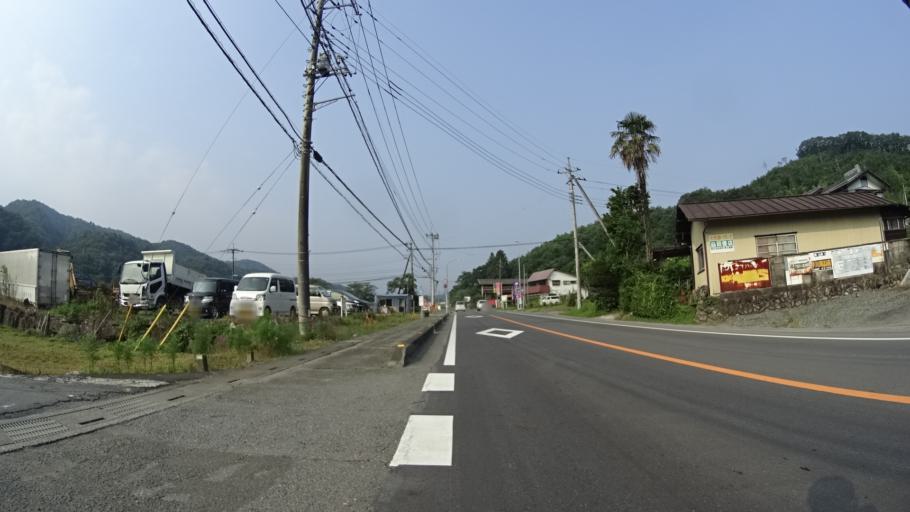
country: JP
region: Saitama
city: Chichibu
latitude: 36.0204
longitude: 139.0655
